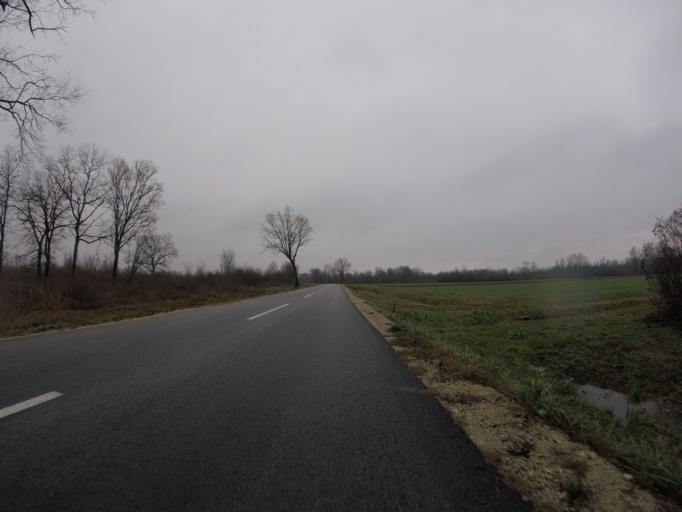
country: HR
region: Zagrebacka
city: Kuce
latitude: 45.7060
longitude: 16.1897
